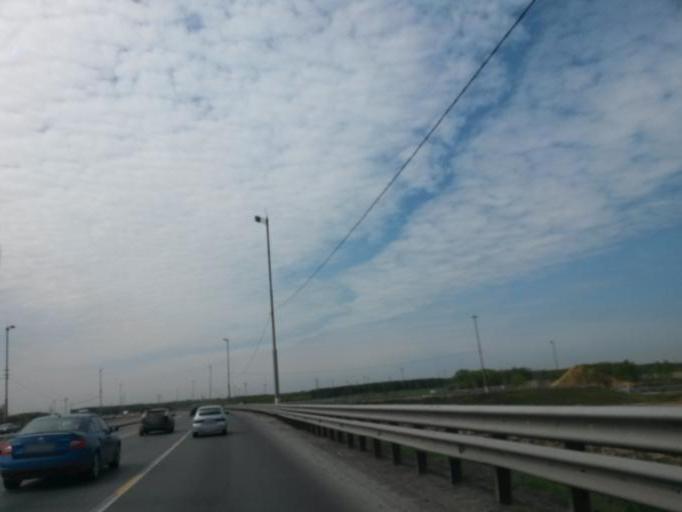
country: RU
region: Moskovskaya
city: L'vovskiy
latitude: 55.3344
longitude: 37.5700
